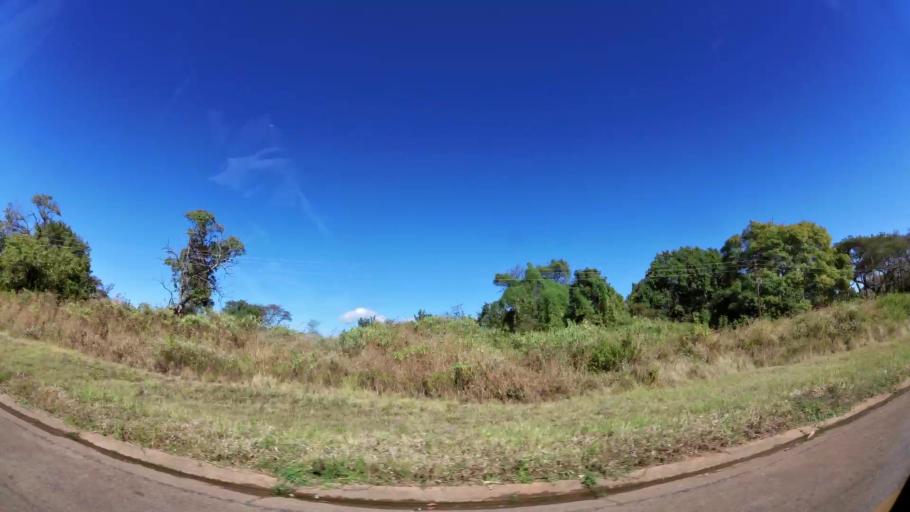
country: ZA
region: Limpopo
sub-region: Mopani District Municipality
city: Tzaneen
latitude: -23.8412
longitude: 30.1414
